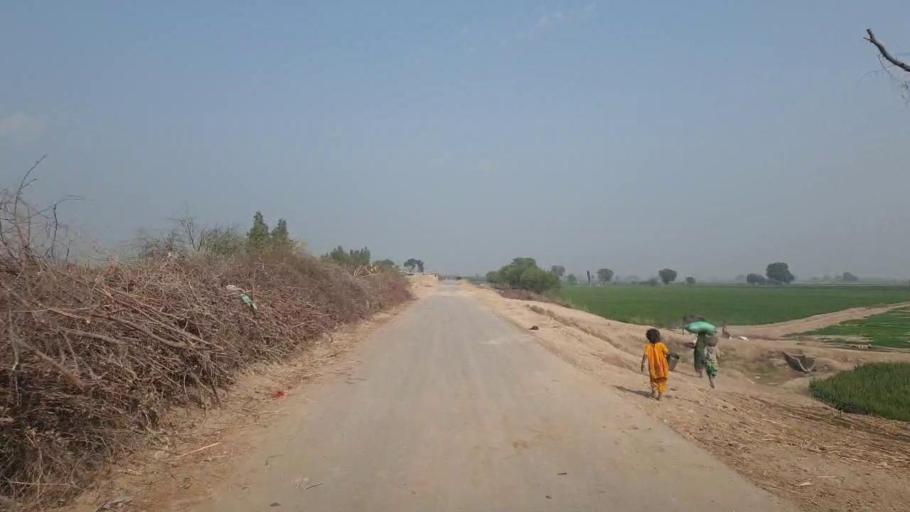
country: PK
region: Sindh
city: Hala
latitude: 25.7795
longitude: 68.3980
